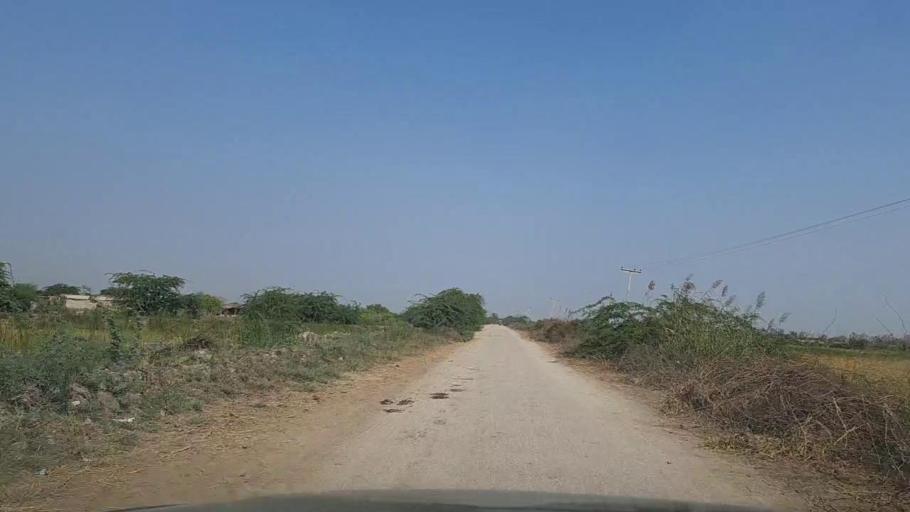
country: PK
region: Sindh
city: Thatta
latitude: 24.5960
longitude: 67.9502
